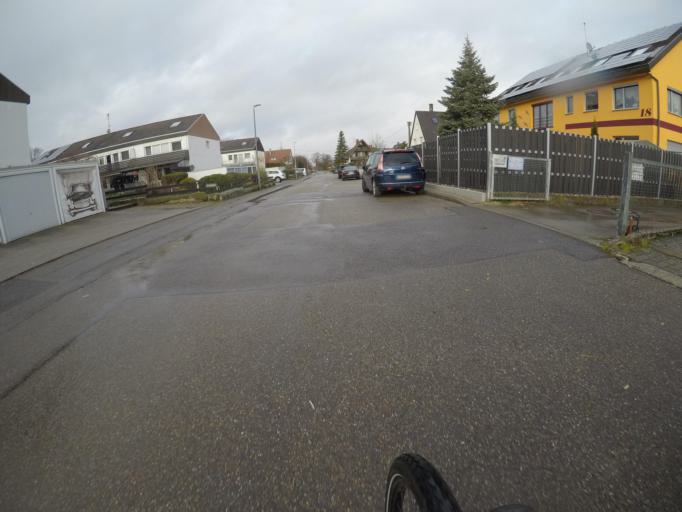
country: DE
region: Baden-Wuerttemberg
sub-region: Regierungsbezirk Stuttgart
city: Eberdingen
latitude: 48.8899
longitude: 8.9989
